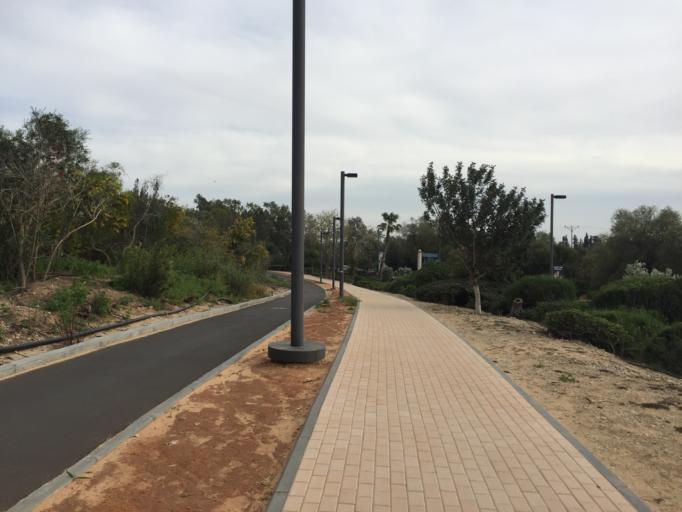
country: IL
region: Haifa
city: Qesarya
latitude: 32.5055
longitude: 34.9041
